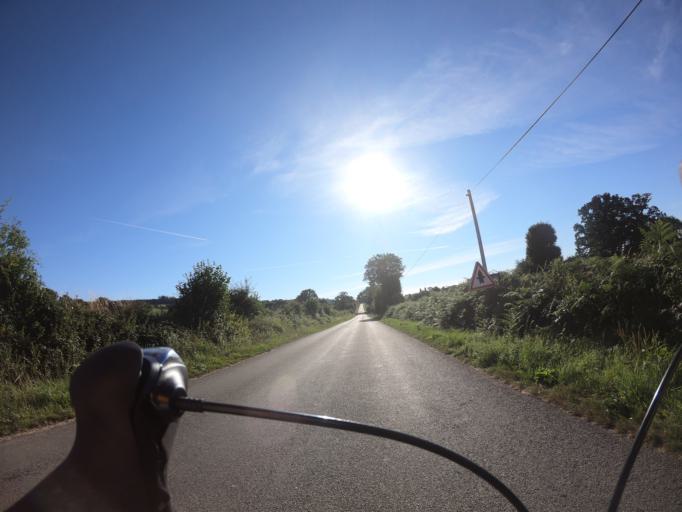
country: FR
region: Pays de la Loire
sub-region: Departement de la Mayenne
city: Pre-en-Pail
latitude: 48.5423
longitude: -0.1987
